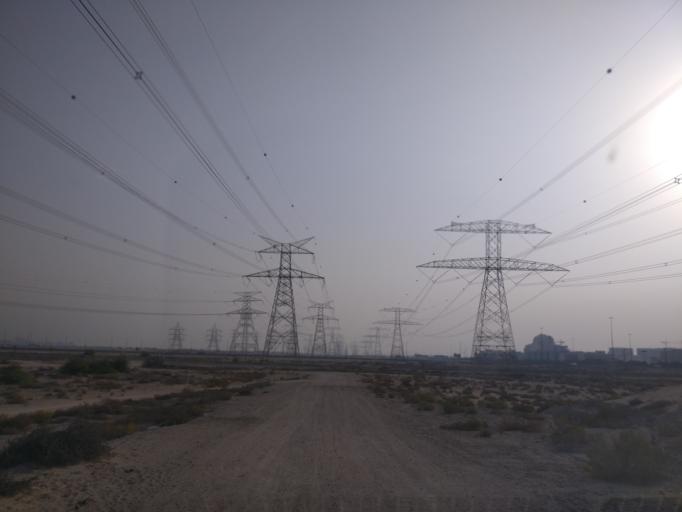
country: AE
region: Dubai
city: Dubai
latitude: 25.0619
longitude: 55.1950
